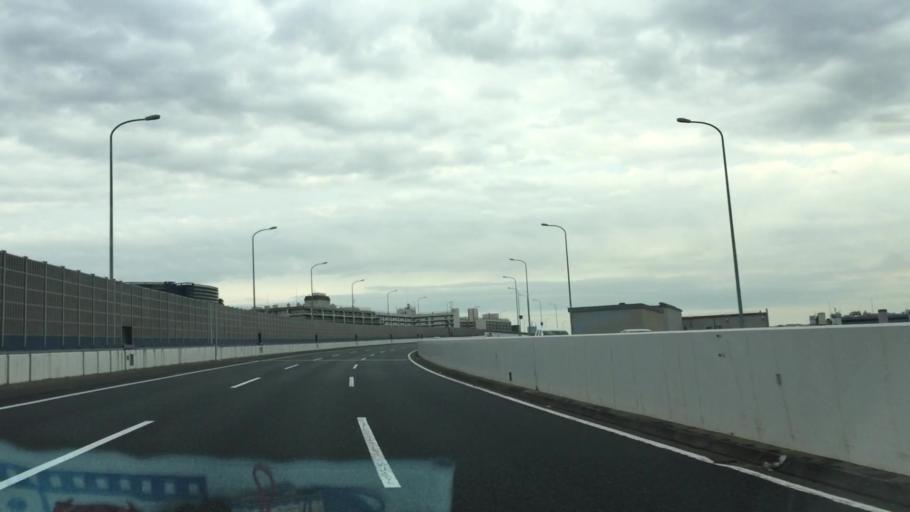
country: JP
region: Kanagawa
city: Yokohama
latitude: 35.3944
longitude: 139.6162
